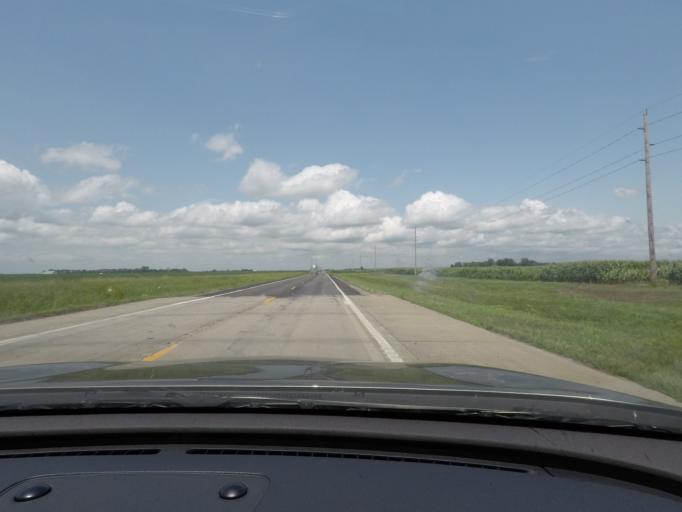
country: US
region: Missouri
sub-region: Carroll County
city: Carrollton
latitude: 39.2324
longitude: -93.5124
